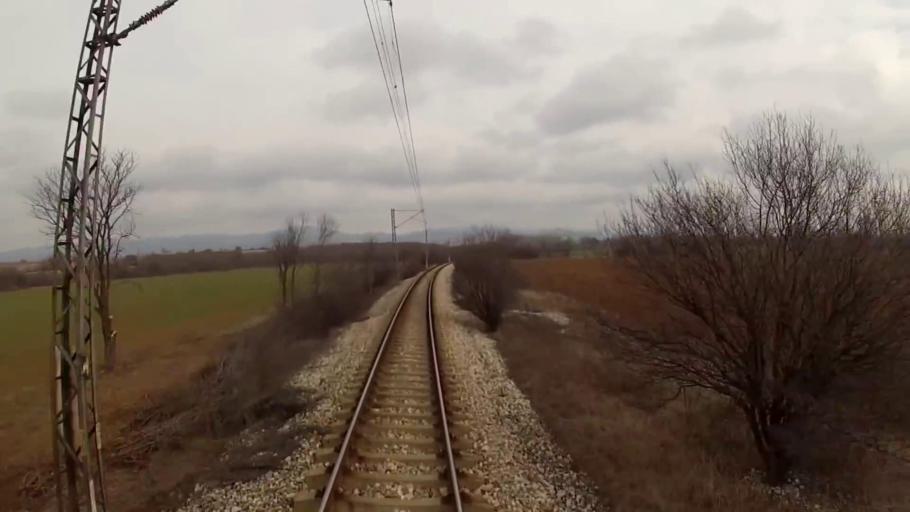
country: BG
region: Sofiya
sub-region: Obshtina Elin Pelin
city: Elin Pelin
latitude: 42.7140
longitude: 23.5812
